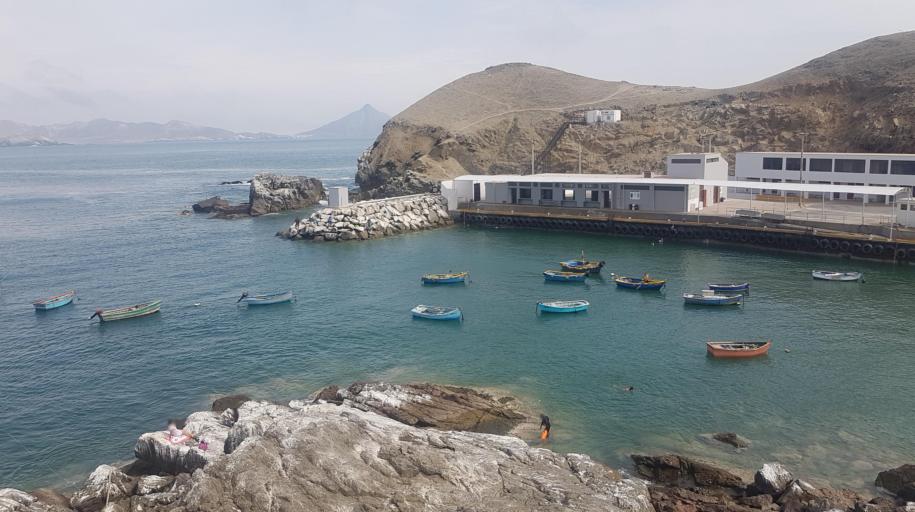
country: PE
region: Ancash
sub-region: Provincia de Santa
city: Samanco
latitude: -9.3273
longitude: -78.4731
